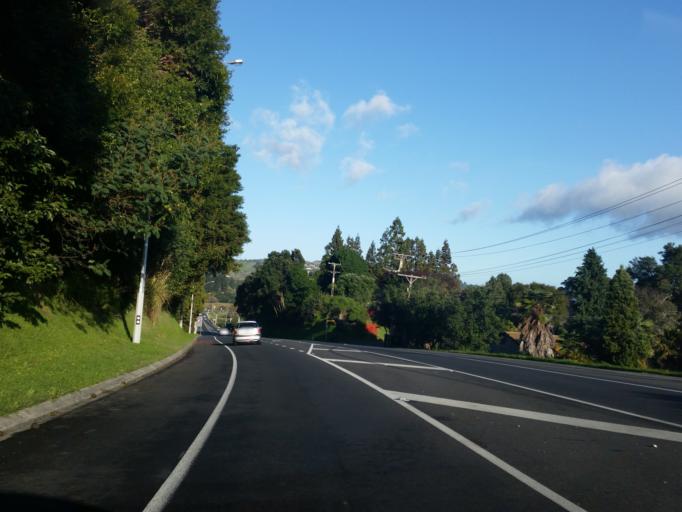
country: NZ
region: Bay of Plenty
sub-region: Tauranga City
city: Tauranga
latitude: -37.6955
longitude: 176.1014
